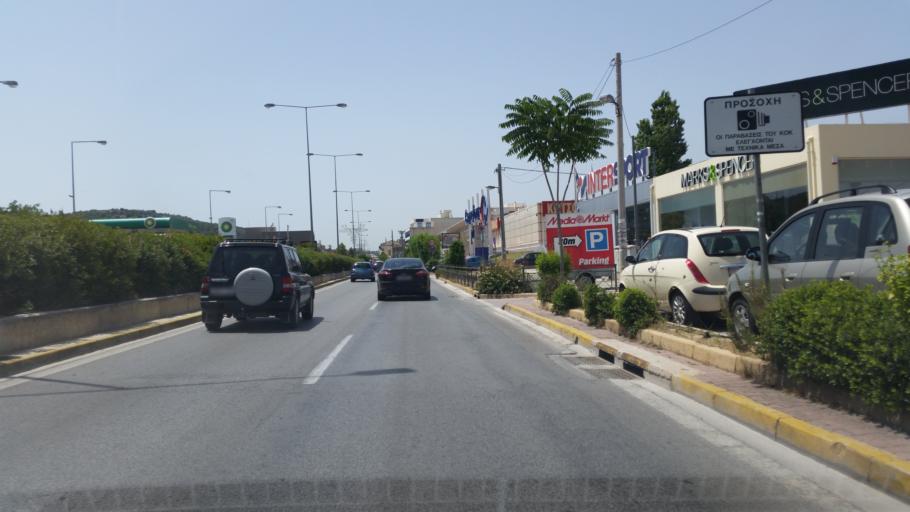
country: GR
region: Attica
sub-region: Nomarchia Anatolikis Attikis
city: Pallini
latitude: 38.0068
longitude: 23.8636
